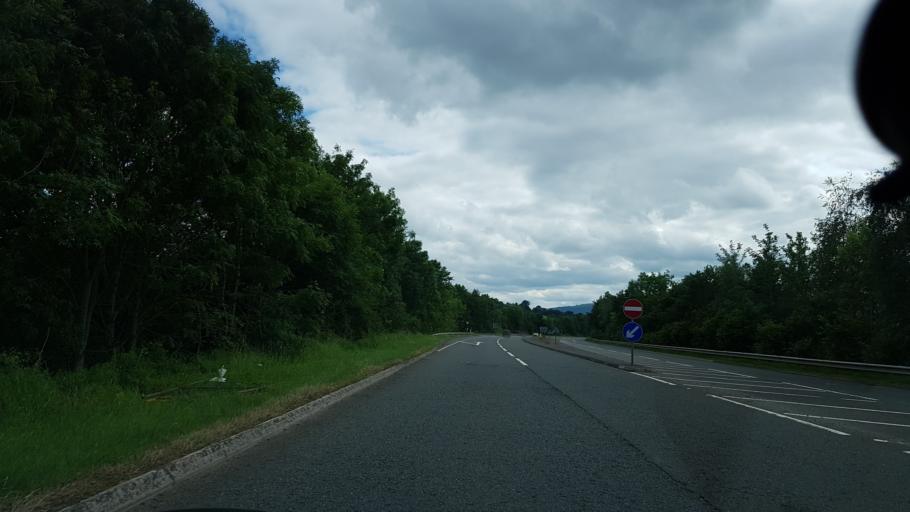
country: GB
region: Wales
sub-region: Monmouthshire
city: Abergavenny
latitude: 51.8361
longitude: -2.9998
